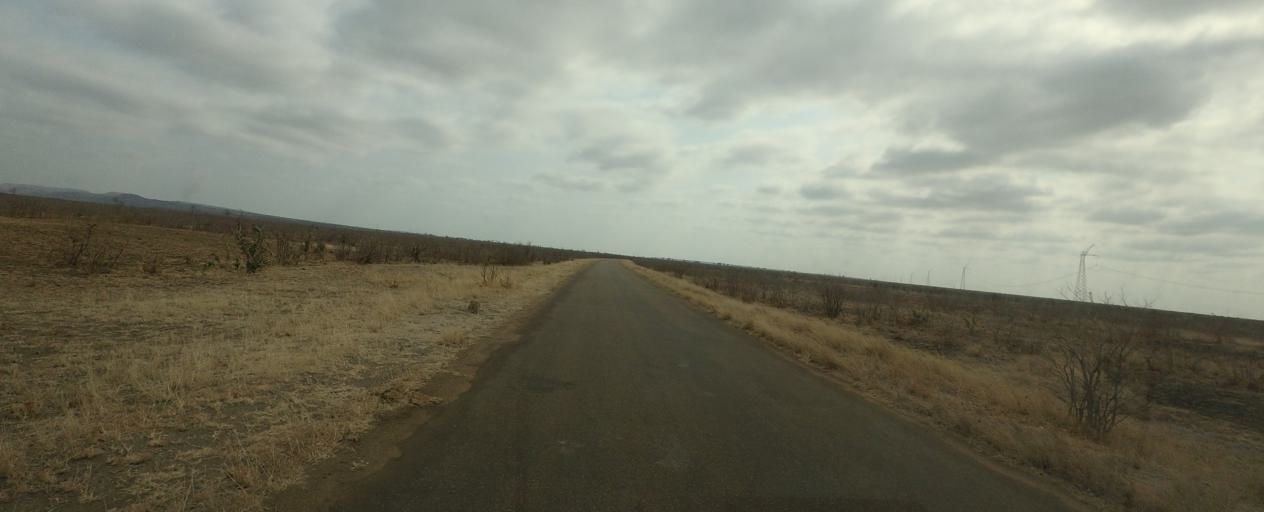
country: ZA
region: Limpopo
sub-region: Vhembe District Municipality
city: Mutale
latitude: -22.6551
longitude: 31.1703
